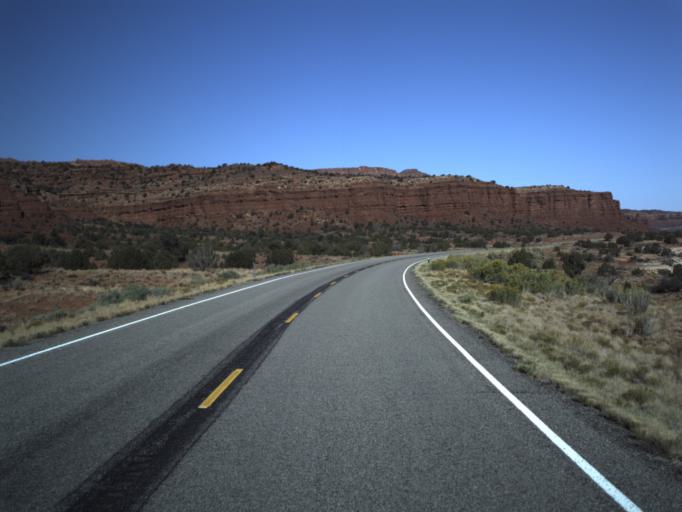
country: US
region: Utah
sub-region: San Juan County
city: Blanding
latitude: 37.6792
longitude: -110.2164
